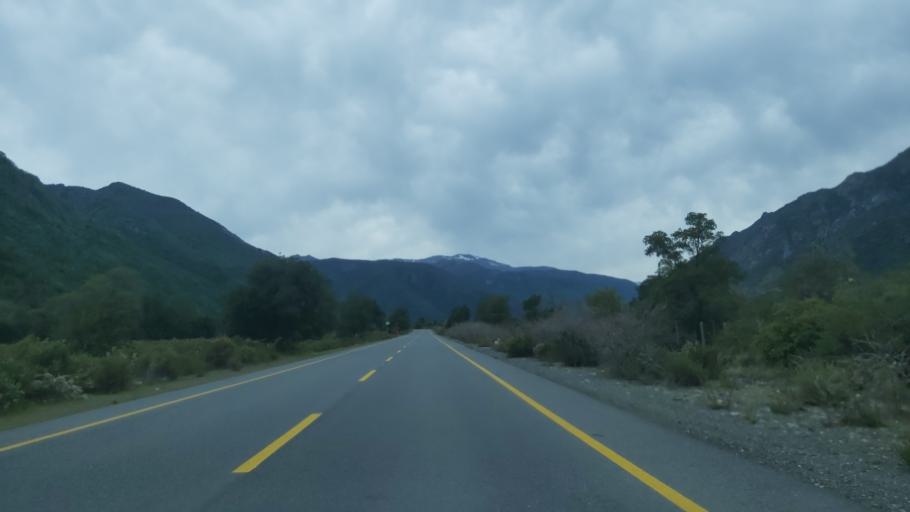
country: CL
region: Maule
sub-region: Provincia de Linares
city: Colbun
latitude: -35.7109
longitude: -71.0647
